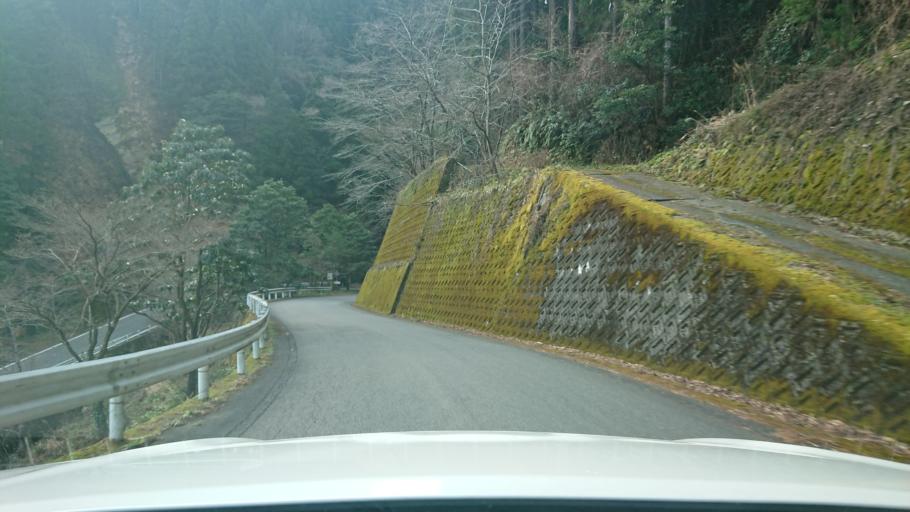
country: JP
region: Tokushima
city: Ishii
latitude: 33.9140
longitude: 134.4155
